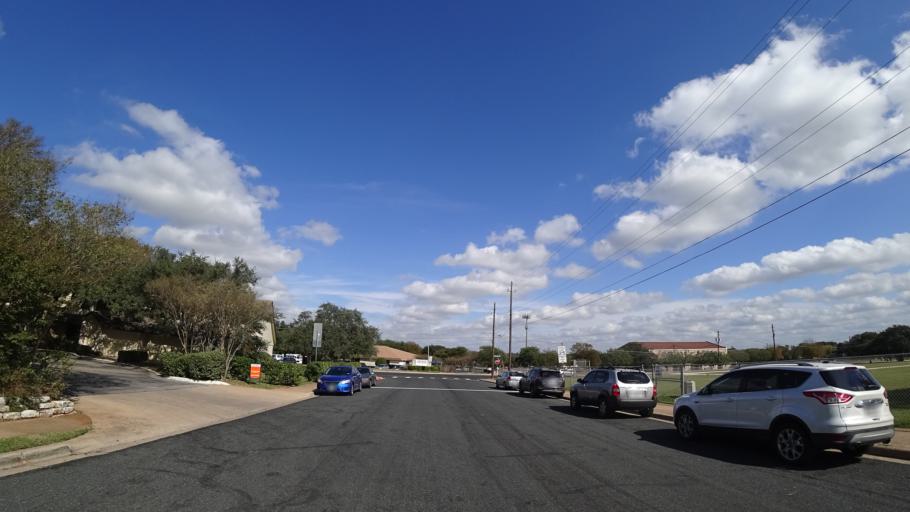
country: US
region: Texas
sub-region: Travis County
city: Wells Branch
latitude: 30.4202
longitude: -97.7191
